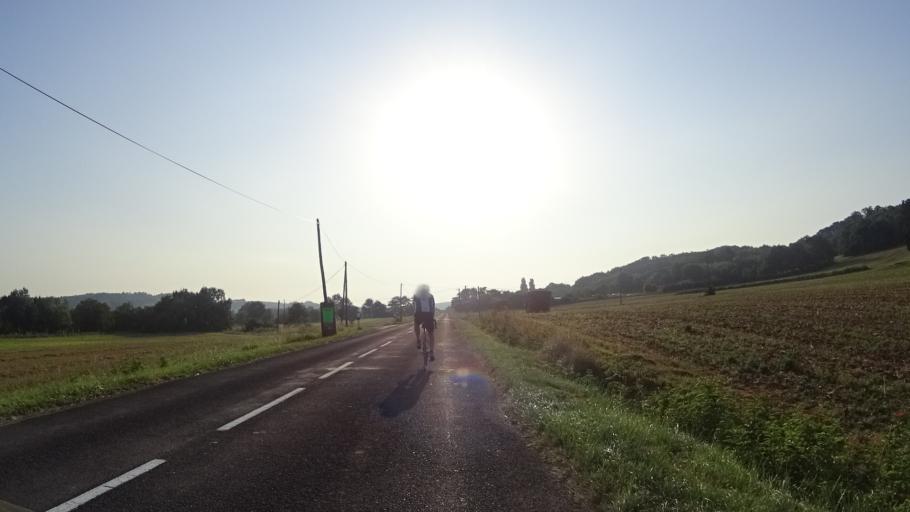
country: FR
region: Midi-Pyrenees
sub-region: Departement de l'Ariege
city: Mirepoix
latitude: 43.0780
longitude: 1.9579
